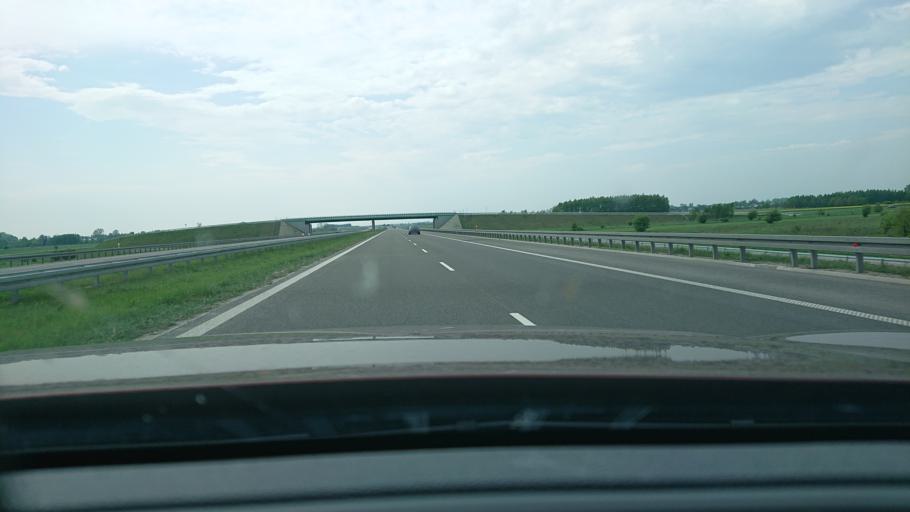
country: PL
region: Subcarpathian Voivodeship
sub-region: Powiat rzeszowski
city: Wolka Podlesna
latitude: 50.0960
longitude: 22.1219
